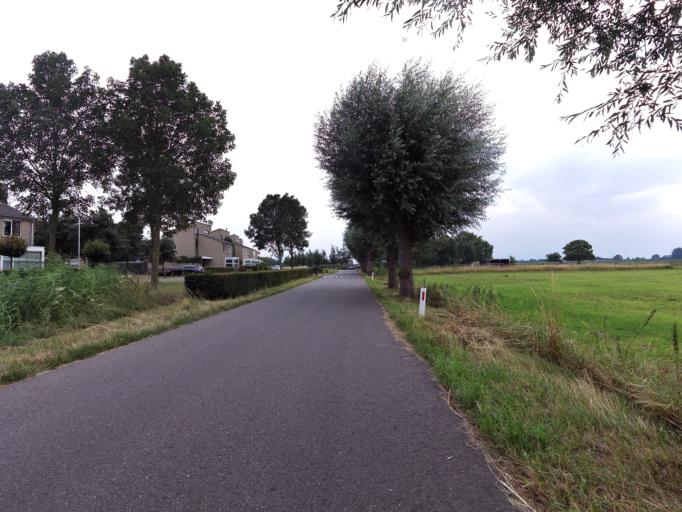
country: NL
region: Gelderland
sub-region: Gemeente Zevenaar
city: Zevenaar
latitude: 51.8623
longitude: 6.0373
